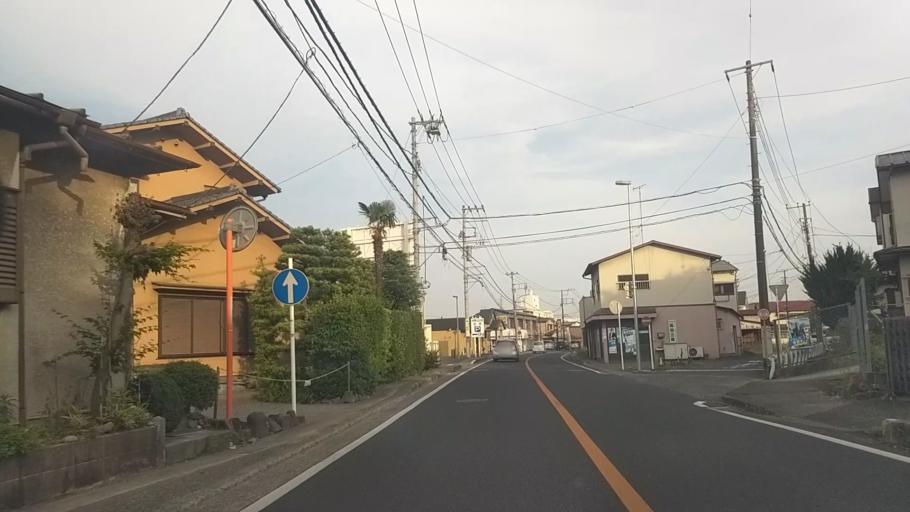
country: JP
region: Kanagawa
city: Odawara
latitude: 35.3010
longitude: 139.1265
